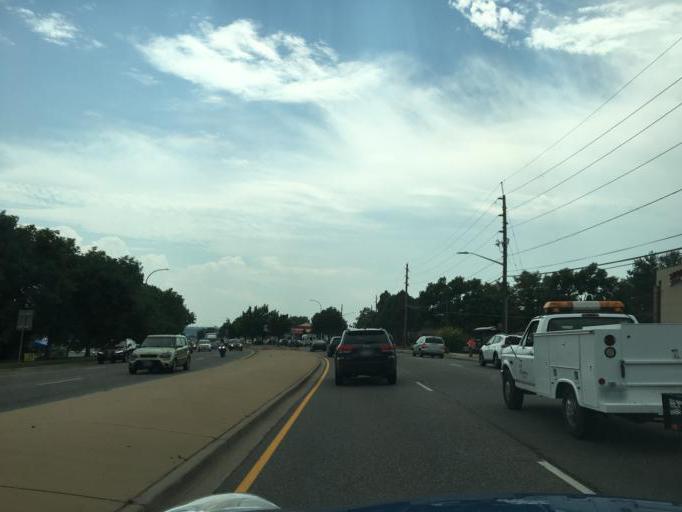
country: US
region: Colorado
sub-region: Jefferson County
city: Arvada
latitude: 39.8156
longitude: -105.0815
